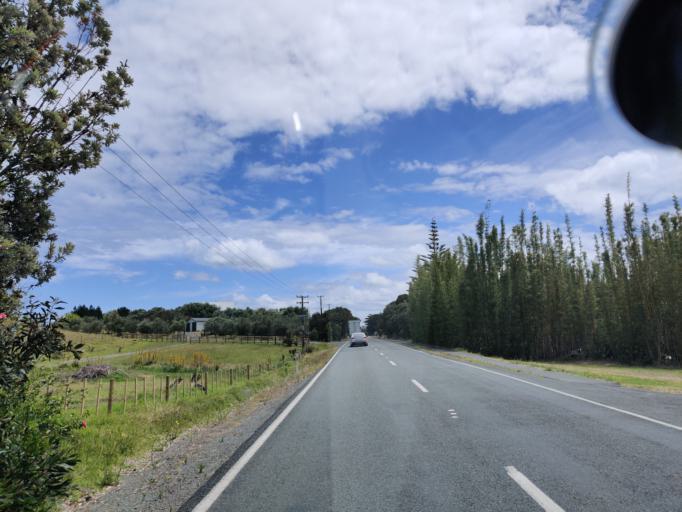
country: NZ
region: Northland
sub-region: Far North District
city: Kaitaia
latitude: -34.8327
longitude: 173.1303
